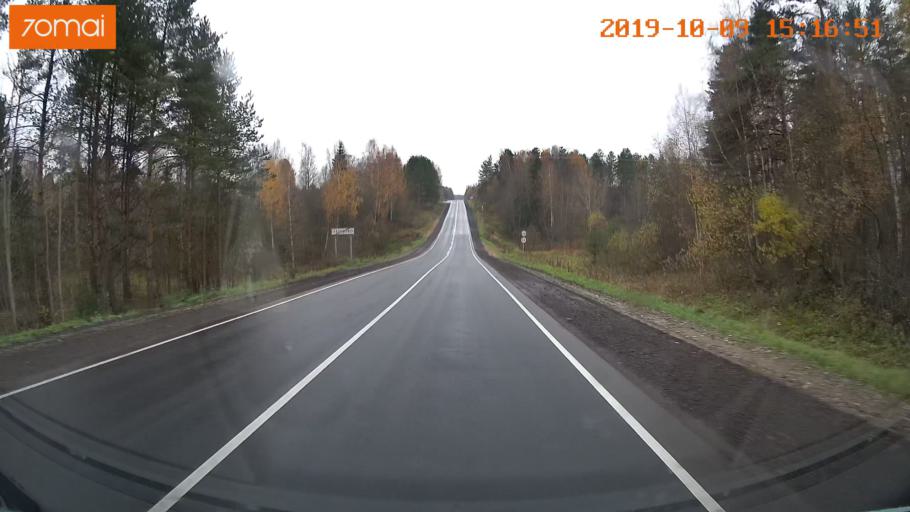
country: RU
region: Kostroma
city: Susanino
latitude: 58.1062
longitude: 41.5849
